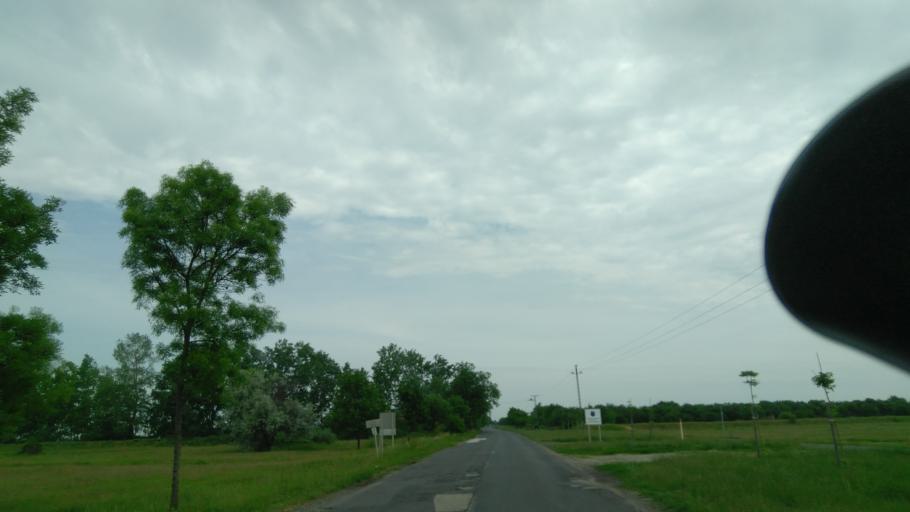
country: HU
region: Bekes
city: Szeghalom
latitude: 47.0361
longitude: 21.1820
